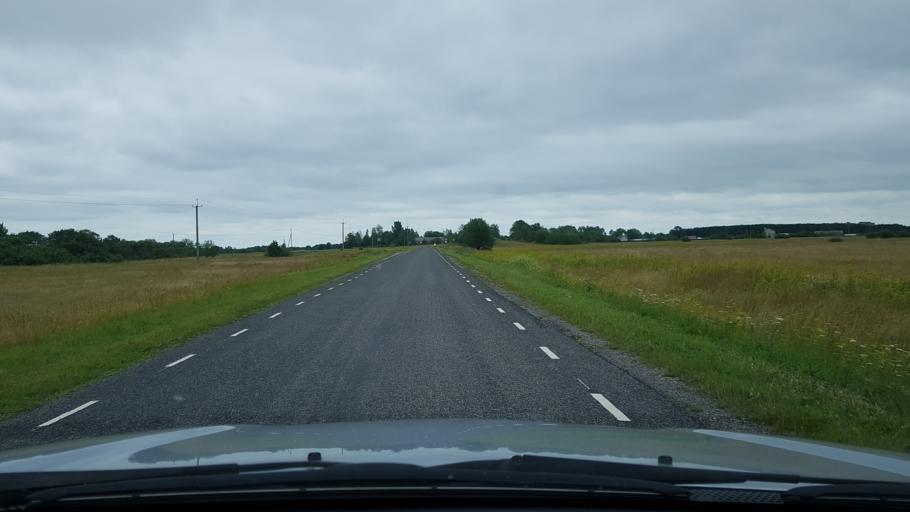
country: EE
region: Ida-Virumaa
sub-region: Narva linn
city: Narva
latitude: 59.3806
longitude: 28.1281
